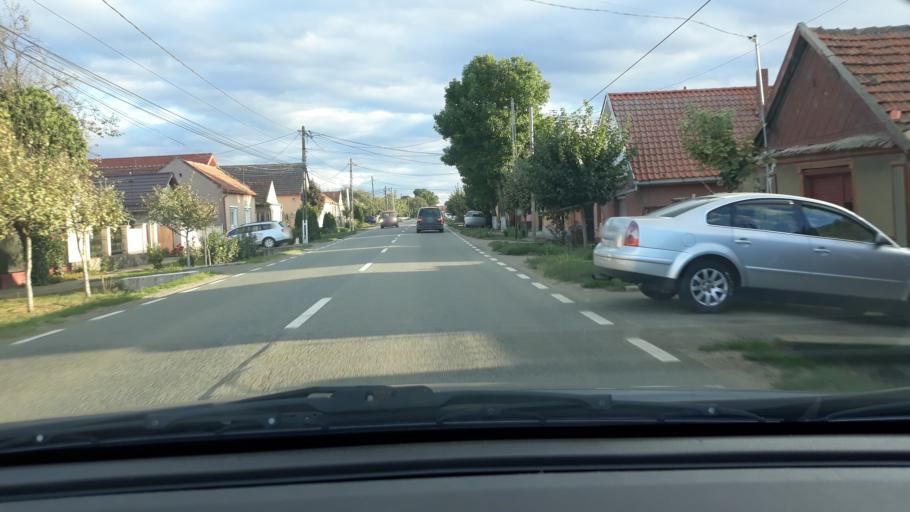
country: RO
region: Bihor
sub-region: Comuna Biharea
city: Biharea
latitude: 47.1626
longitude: 21.9222
